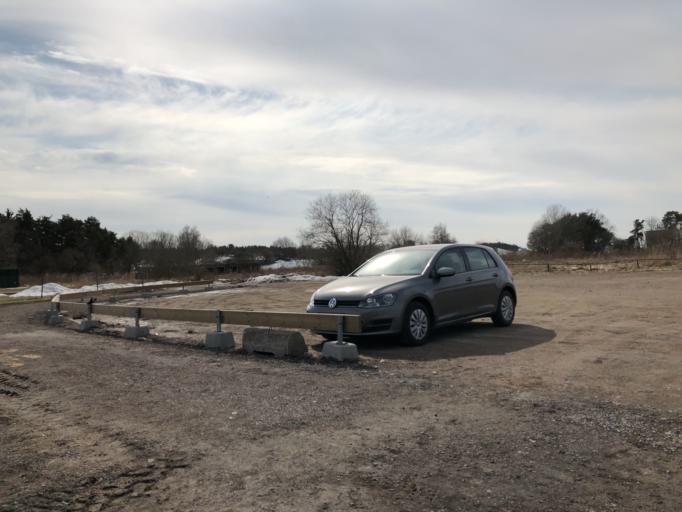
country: SE
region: Kalmar
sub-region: Kalmar Kommun
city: Kalmar
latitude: 56.6613
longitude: 16.3160
